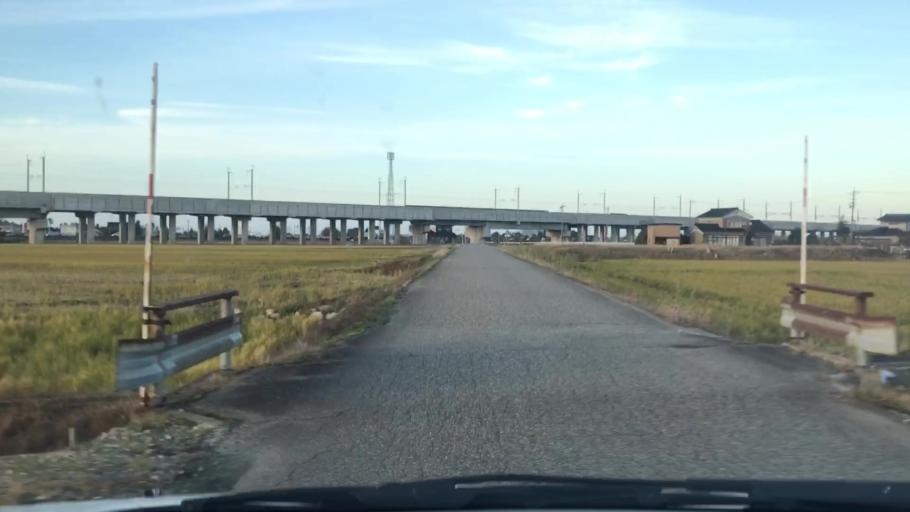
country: JP
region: Toyama
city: Namerikawa
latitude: 36.7298
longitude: 137.3357
